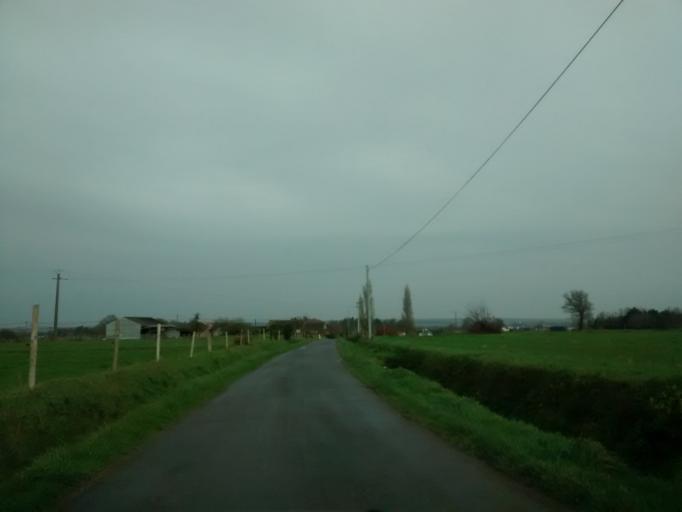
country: FR
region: Brittany
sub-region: Departement d'Ille-et-Vilaine
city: Noyal-sur-Vilaine
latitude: 48.1055
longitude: -1.5400
